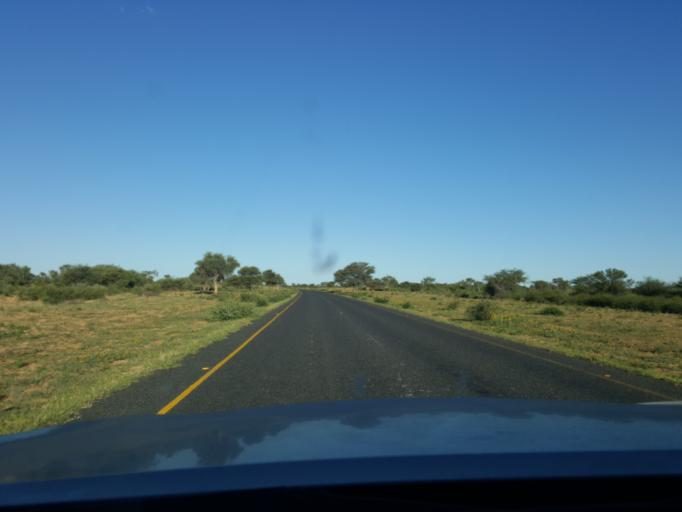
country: BW
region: Southern
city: Khakhea
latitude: -24.2520
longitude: 23.2951
